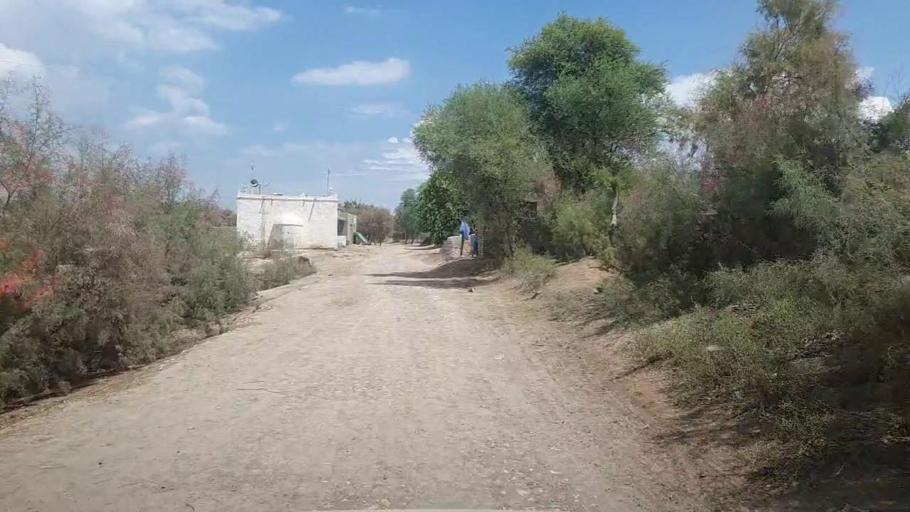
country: PK
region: Sindh
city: Kandhkot
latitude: 28.3400
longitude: 69.2526
